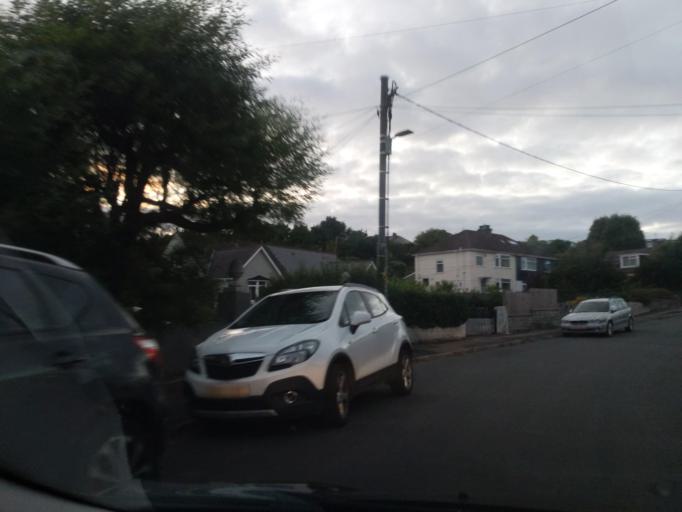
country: GB
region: England
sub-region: Plymouth
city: Plymstock
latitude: 50.3582
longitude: -4.0999
